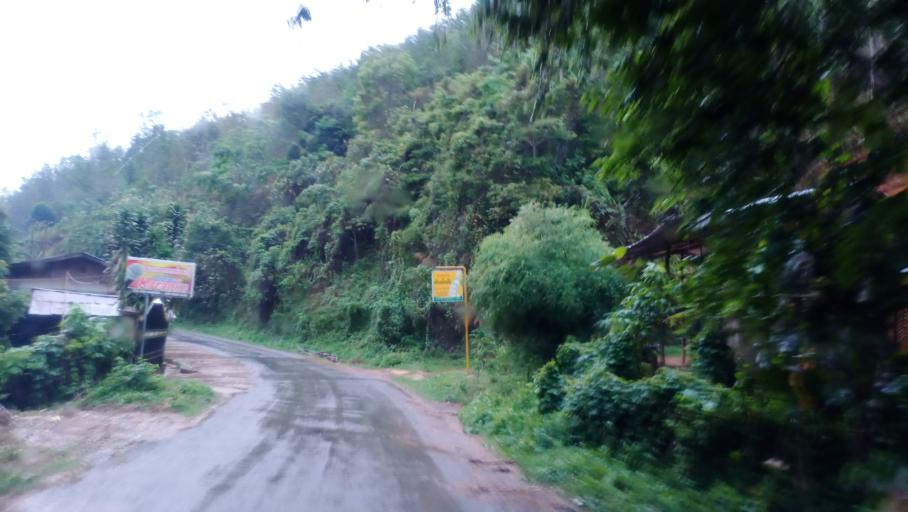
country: LA
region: Phongsali
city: Khoa
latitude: 21.0699
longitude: 102.4915
